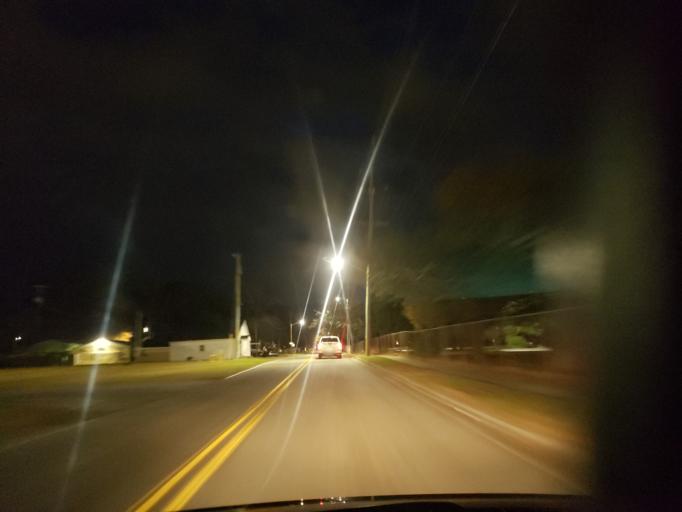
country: US
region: Georgia
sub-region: Chatham County
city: Thunderbolt
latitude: 32.0648
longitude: -81.0581
